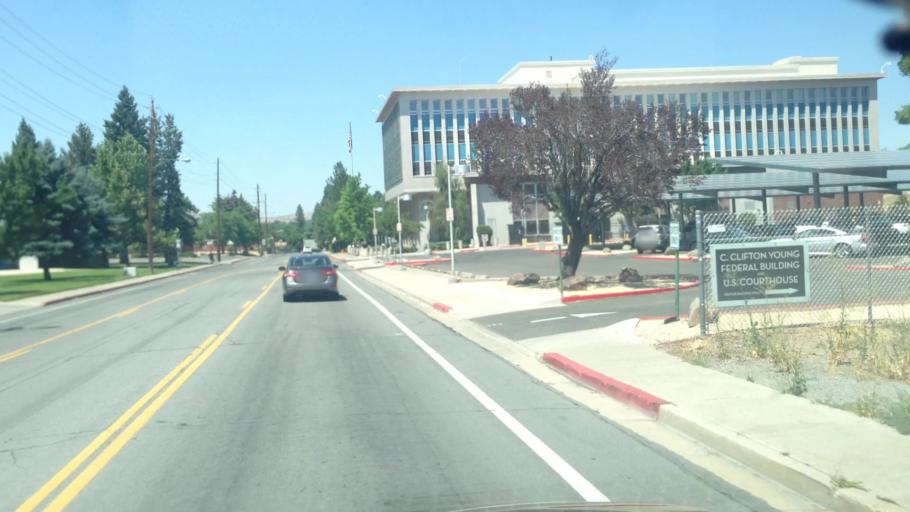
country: US
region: Nevada
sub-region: Washoe County
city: Reno
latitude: 39.5168
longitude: -119.8264
